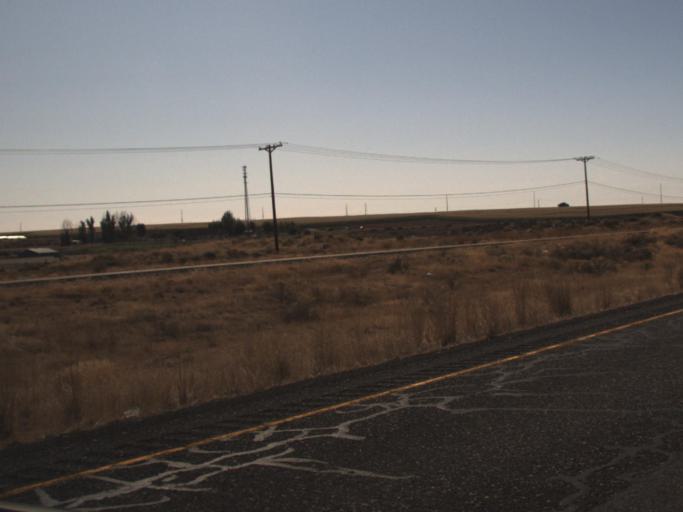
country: US
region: Washington
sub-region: Franklin County
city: Basin City
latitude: 46.4403
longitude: -119.0213
